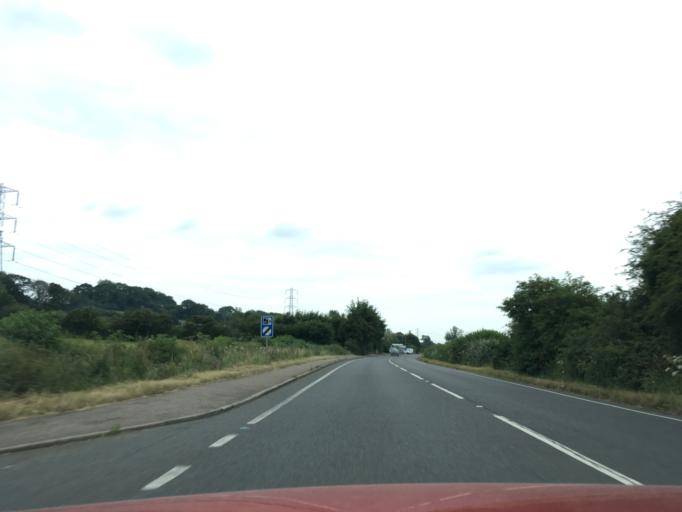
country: GB
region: England
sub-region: Central Bedfordshire
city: Kensworth
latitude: 51.8626
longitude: -0.4843
